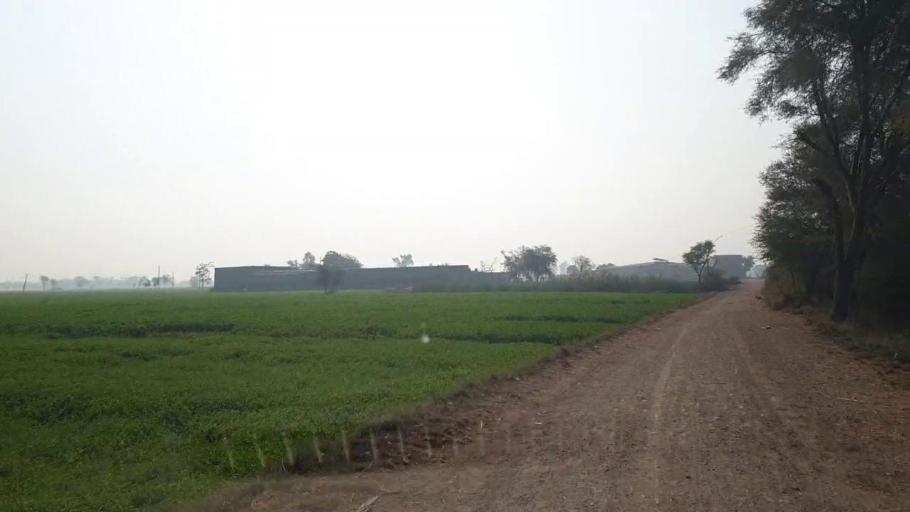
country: PK
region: Sindh
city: Sakrand
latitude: 26.0004
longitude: 68.3674
